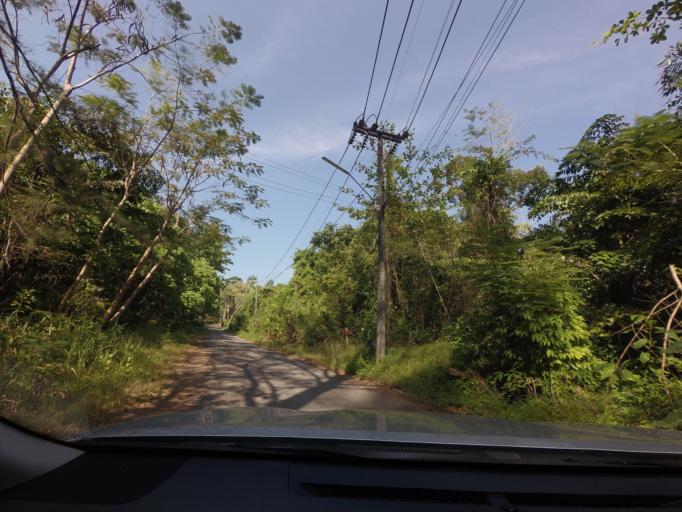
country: TH
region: Phangnga
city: Ban Khao Lak
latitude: 8.7394
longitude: 98.2466
